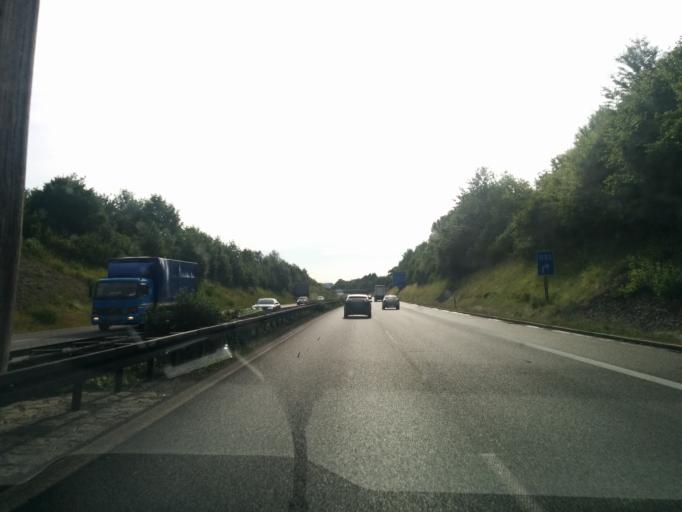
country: DE
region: Bavaria
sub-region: Upper Bavaria
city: Greifenberg
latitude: 48.0733
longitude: 11.0828
